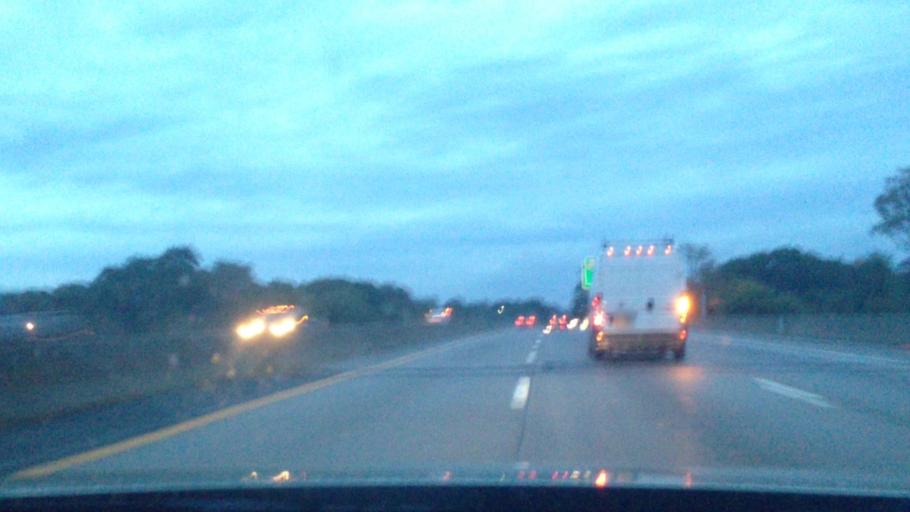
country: US
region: New York
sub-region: Suffolk County
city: Islip
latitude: 40.7413
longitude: -73.2149
